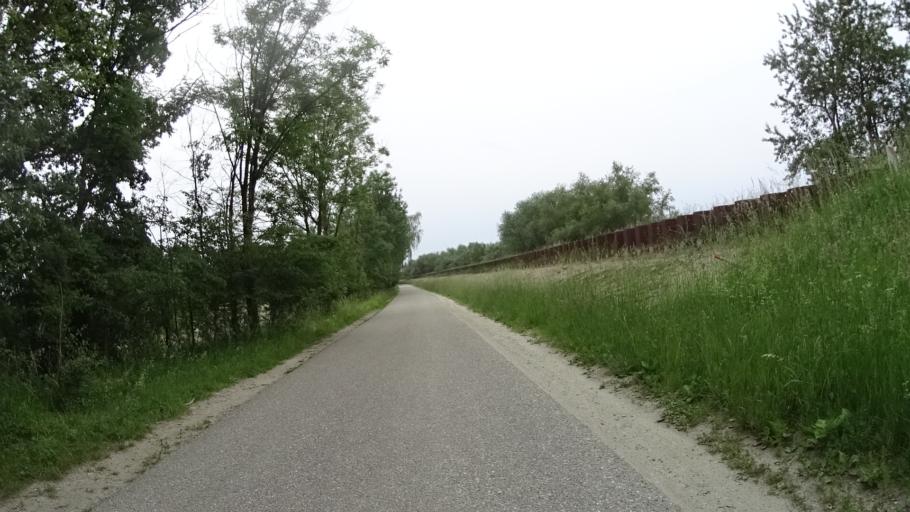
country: DE
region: Bavaria
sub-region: Lower Bavaria
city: Niederalteich
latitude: 48.7771
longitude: 13.0087
